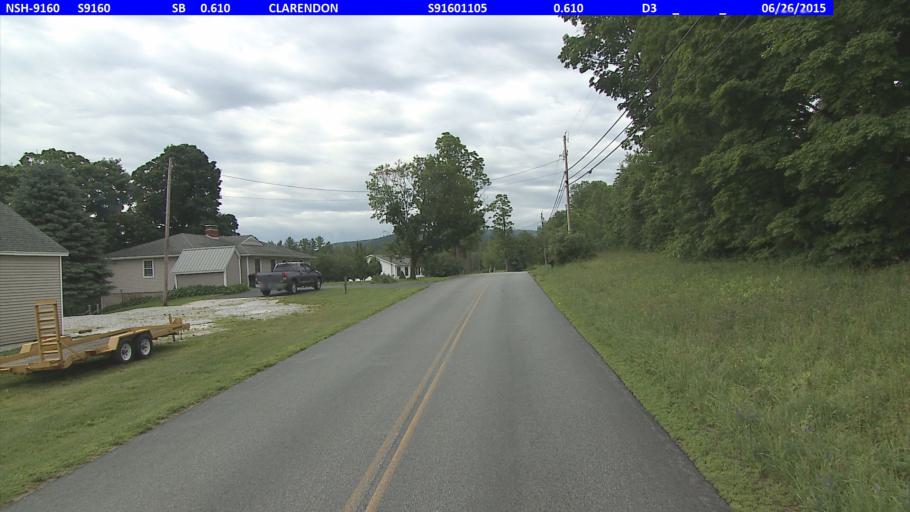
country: US
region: Vermont
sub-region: Rutland County
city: Rutland
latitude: 43.5363
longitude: -72.9468
